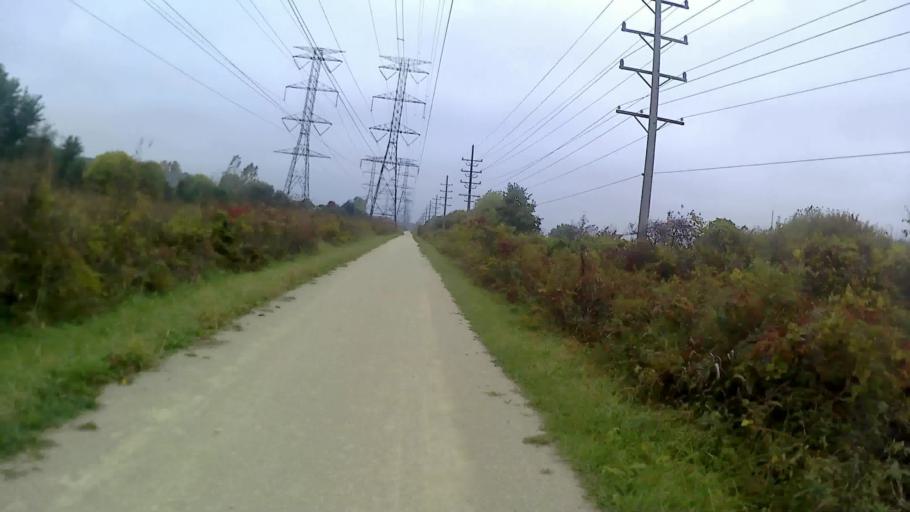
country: US
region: Illinois
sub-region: Kane County
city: Aurora
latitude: 41.7932
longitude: -88.2548
